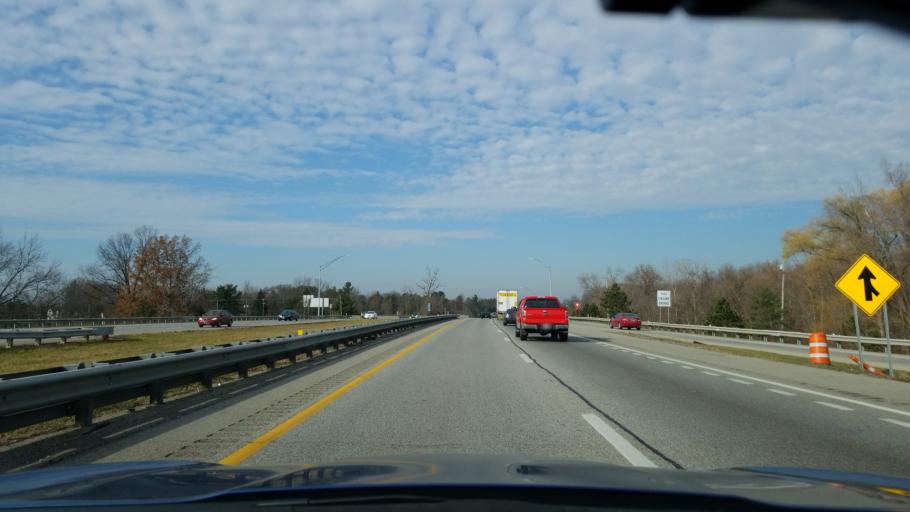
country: US
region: Ohio
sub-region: Cuyahoga County
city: Solon
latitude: 41.4082
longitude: -81.4690
